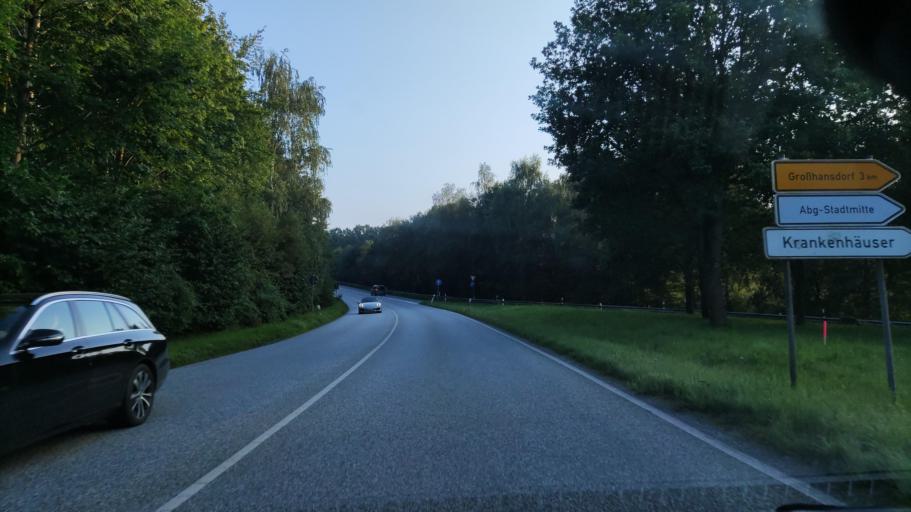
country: DE
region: Schleswig-Holstein
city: Ahrensburg
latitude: 53.6621
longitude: 10.2494
